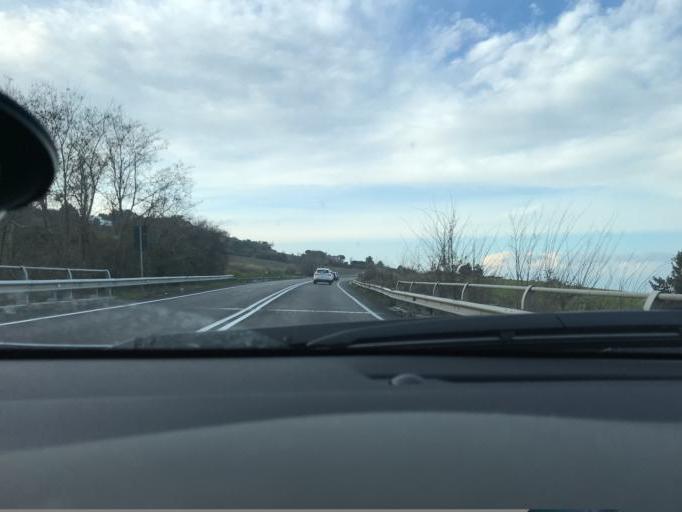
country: IT
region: The Marches
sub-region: Provincia di Ancona
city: Falconara Marittima
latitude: 43.6051
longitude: 13.4194
